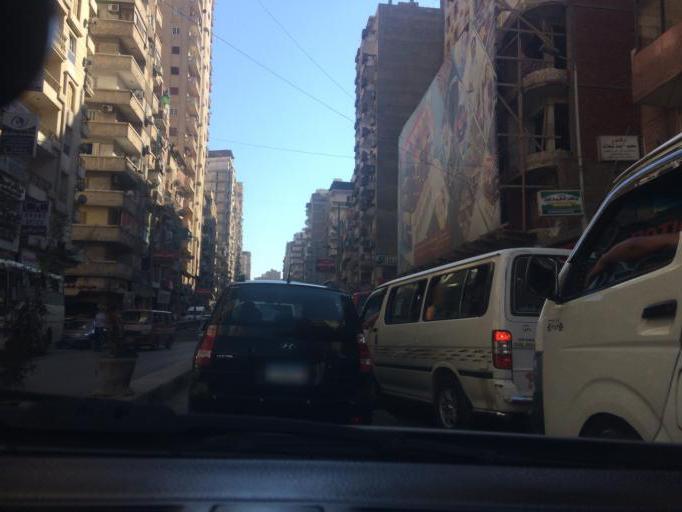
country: EG
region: Alexandria
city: Alexandria
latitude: 31.2598
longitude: 29.9900
